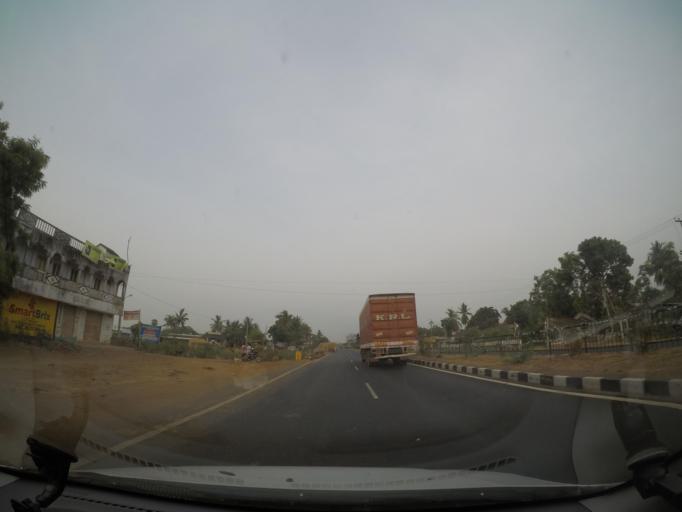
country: IN
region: Andhra Pradesh
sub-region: Krishna
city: Gannavaram
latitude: 16.6094
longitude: 80.9091
